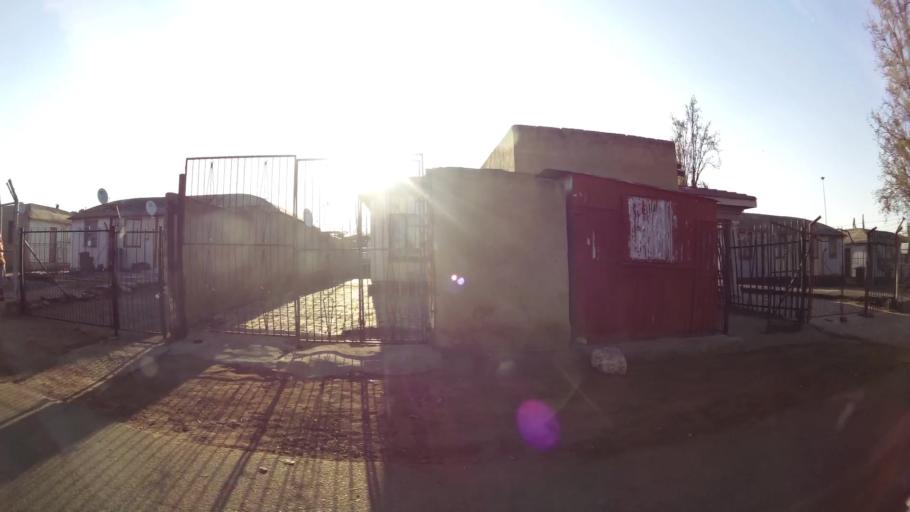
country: ZA
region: Gauteng
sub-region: City of Johannesburg Metropolitan Municipality
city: Soweto
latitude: -26.2535
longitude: 27.8830
